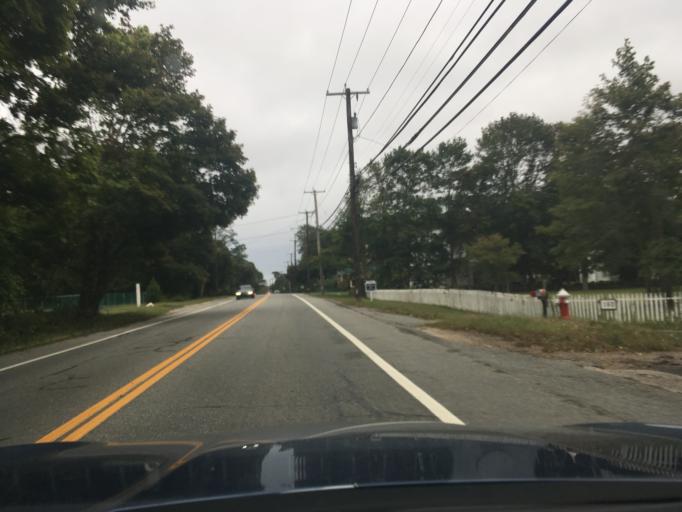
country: US
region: Rhode Island
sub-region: Washington County
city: North Kingstown
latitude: 41.5676
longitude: -71.4698
